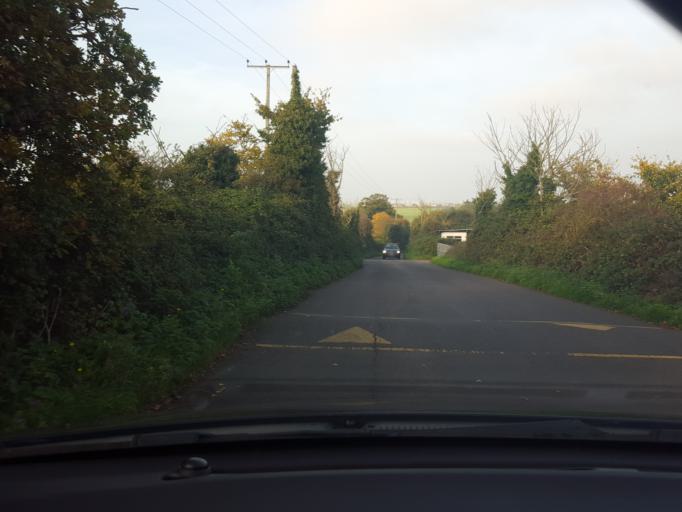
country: GB
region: England
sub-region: Essex
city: Walton-on-the-Naze
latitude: 51.8518
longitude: 1.2564
